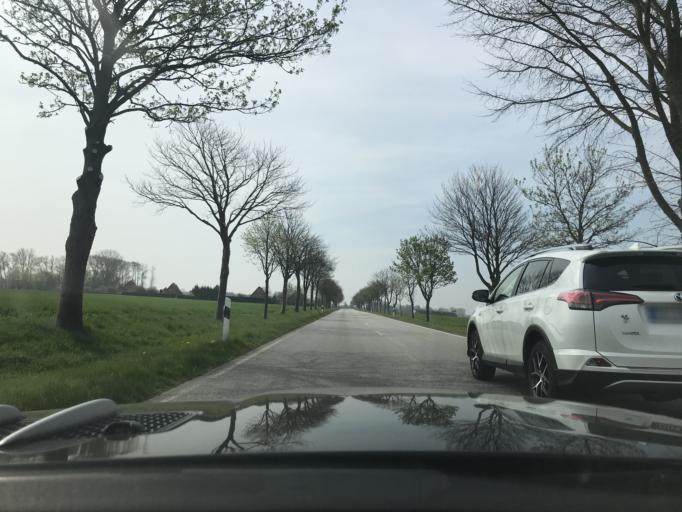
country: DE
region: Schleswig-Holstein
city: Grube
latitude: 54.2501
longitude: 11.0313
